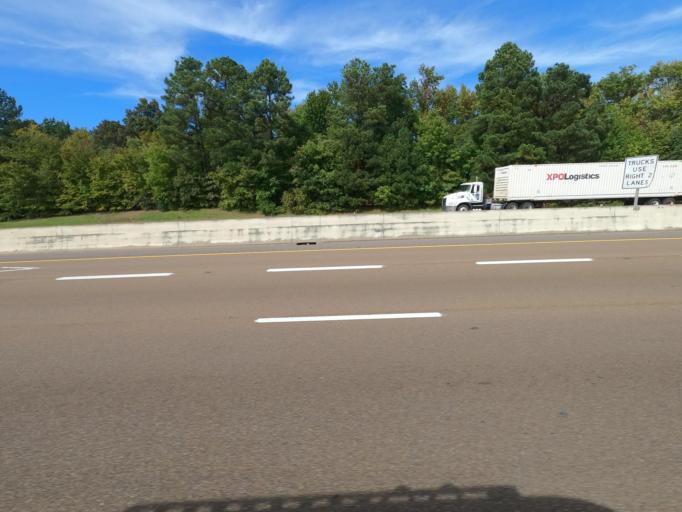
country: US
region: Tennessee
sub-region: Shelby County
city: Lakeland
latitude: 35.1971
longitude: -89.7867
